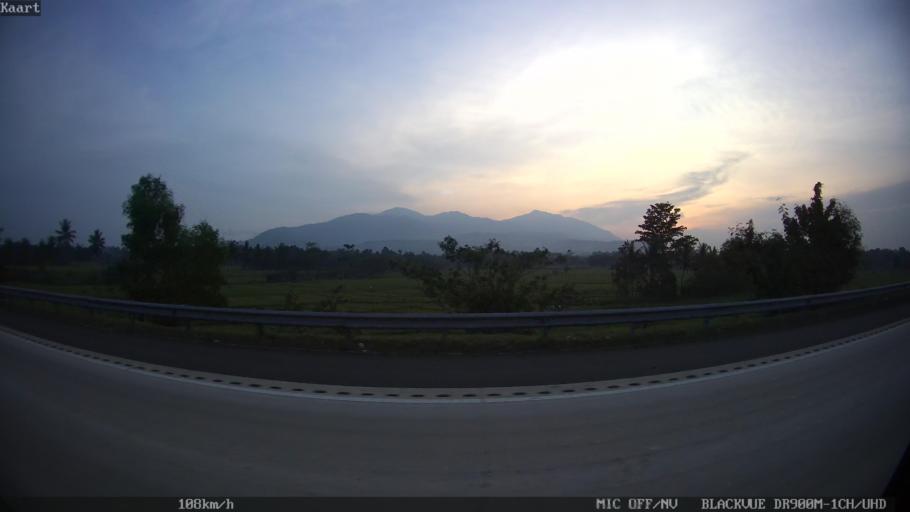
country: ID
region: Lampung
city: Penengahan
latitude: -5.7551
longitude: 105.7096
